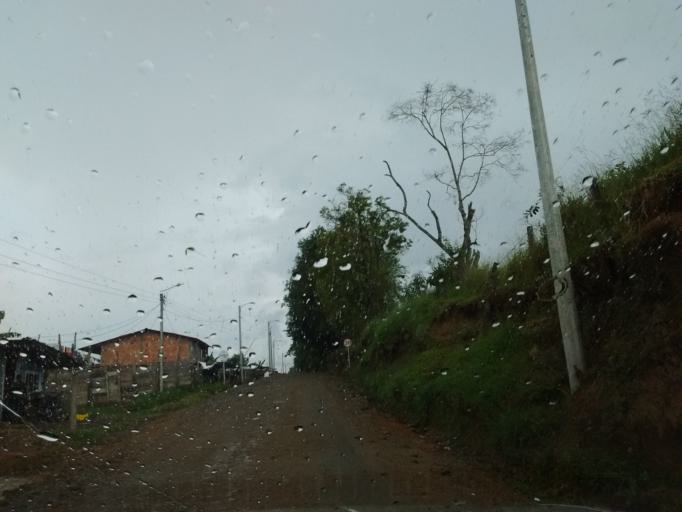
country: CO
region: Cauca
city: Popayan
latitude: 2.5178
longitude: -76.5911
